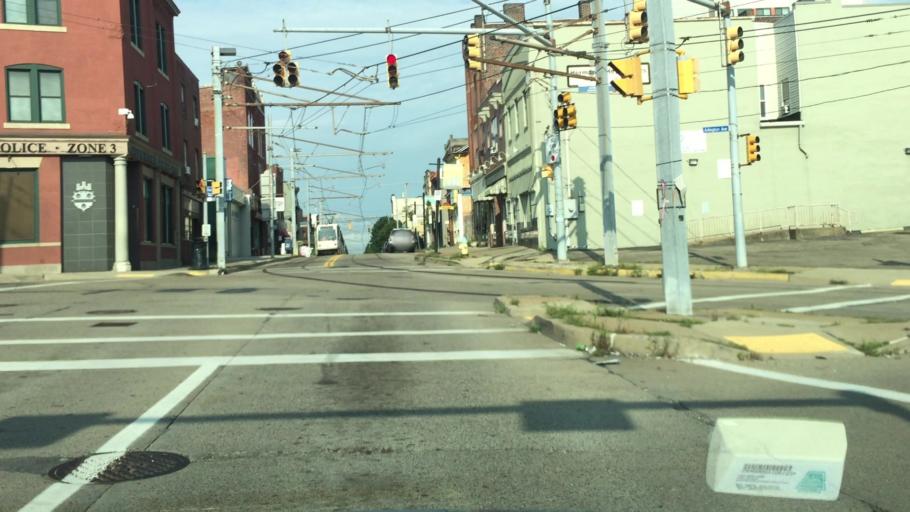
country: US
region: Pennsylvania
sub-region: Allegheny County
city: Mount Oliver
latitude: 40.4218
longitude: -79.9920
